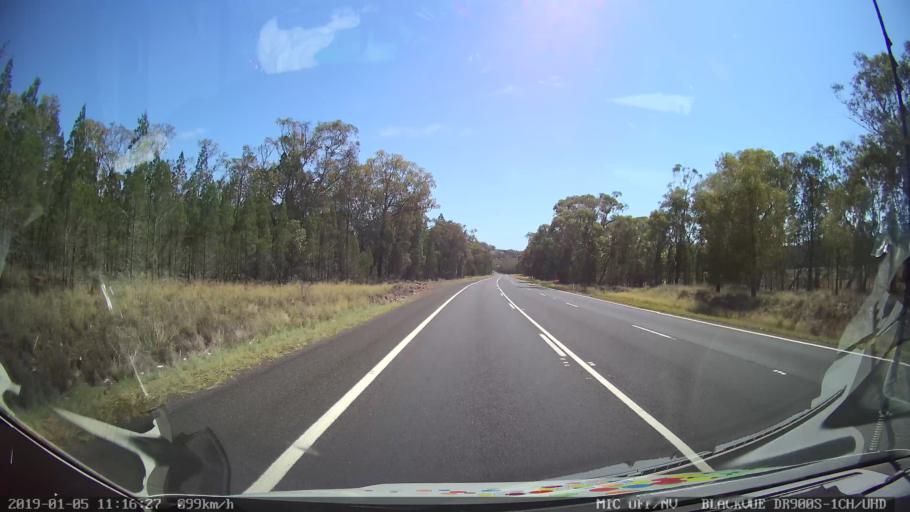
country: AU
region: New South Wales
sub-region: Warrumbungle Shire
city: Coonabarabran
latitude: -31.3386
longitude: 149.2983
